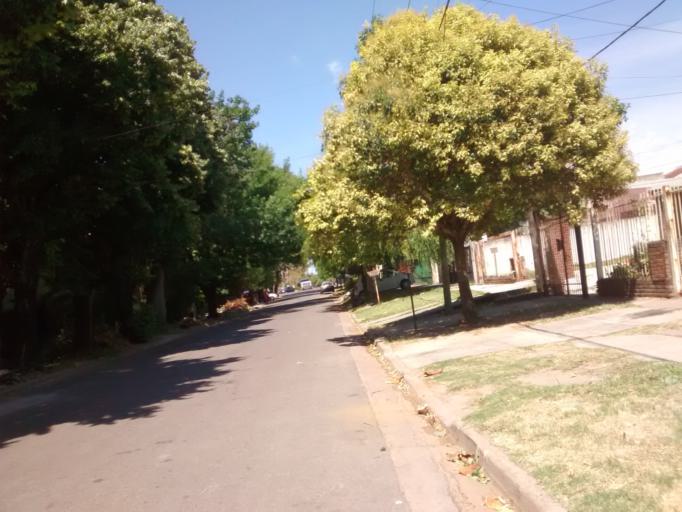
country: AR
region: Buenos Aires
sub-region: Partido de La Plata
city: La Plata
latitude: -34.8826
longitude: -58.0048
